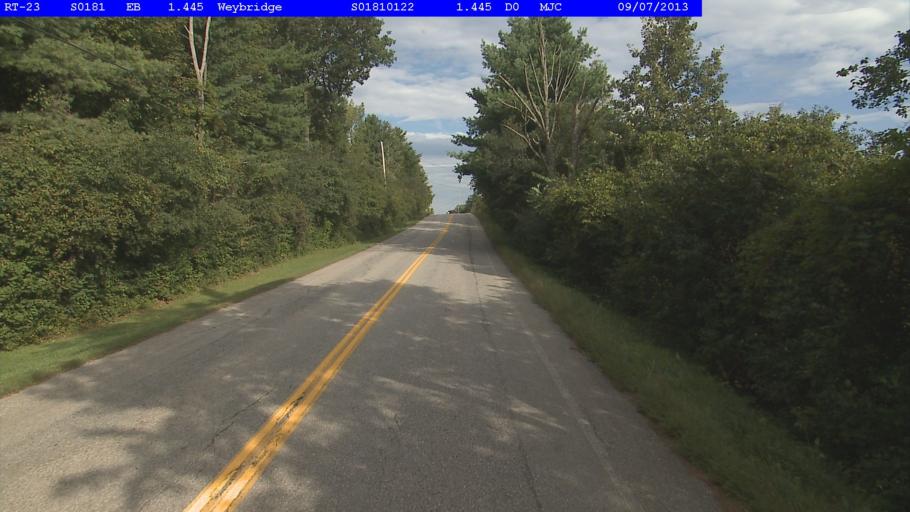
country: US
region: Vermont
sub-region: Addison County
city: Middlebury (village)
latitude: 44.0328
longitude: -73.2038
